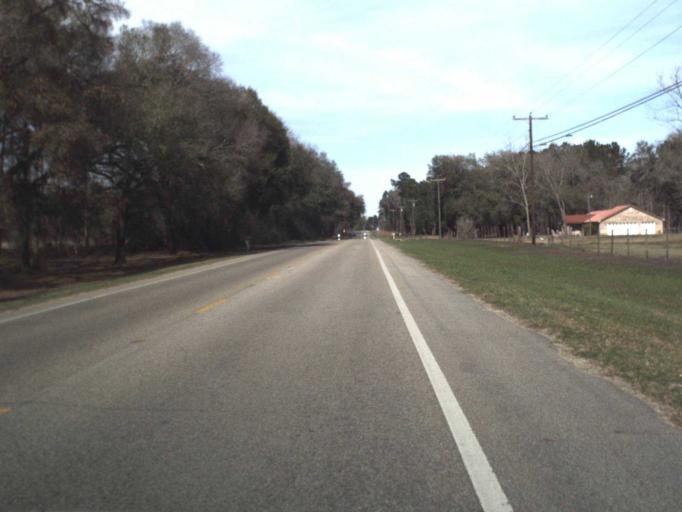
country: US
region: Florida
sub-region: Jackson County
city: Graceville
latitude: 30.9244
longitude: -85.5198
